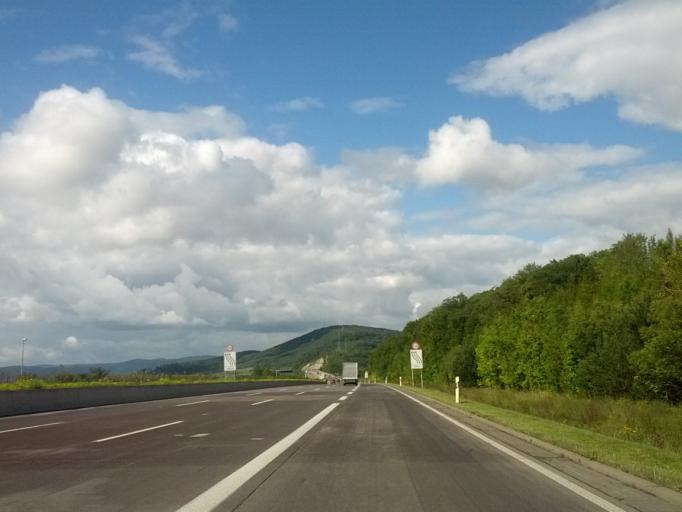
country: DE
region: Thuringia
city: Krauthausen
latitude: 51.0084
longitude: 10.2453
